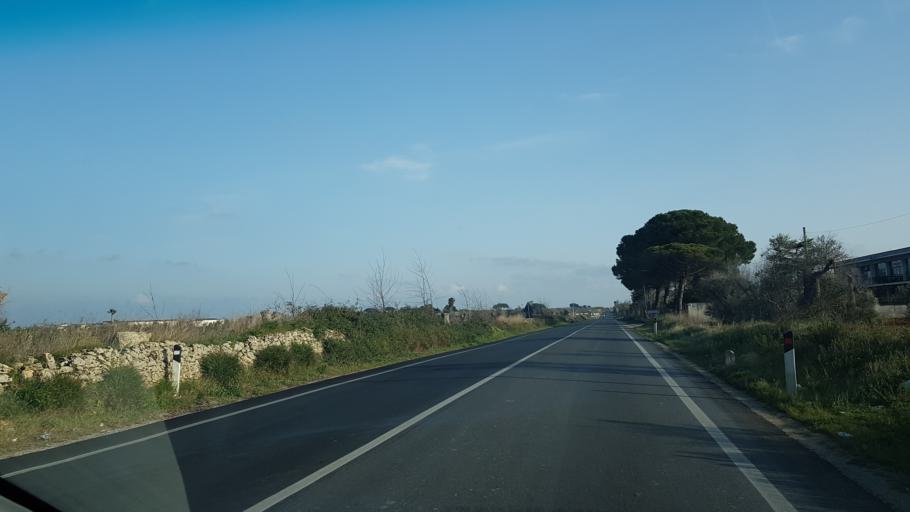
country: IT
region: Apulia
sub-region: Provincia di Lecce
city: Squinzano
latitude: 40.4237
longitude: 18.0562
